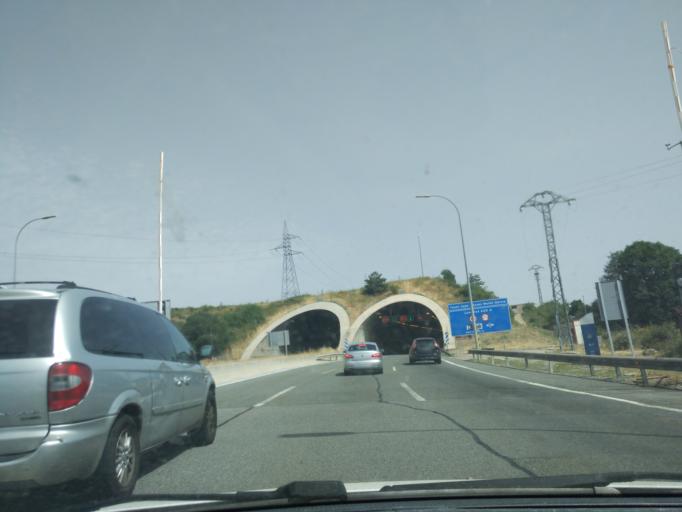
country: ES
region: Madrid
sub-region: Provincia de Madrid
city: Somosierra
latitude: 41.1305
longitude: -3.5840
